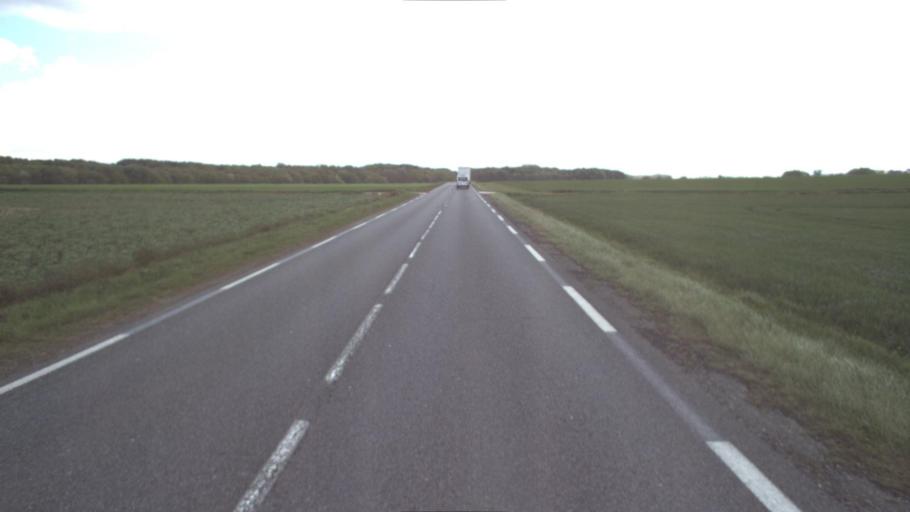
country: FR
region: Ile-de-France
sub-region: Departement de Seine-et-Marne
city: Jouy-le-Chatel
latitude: 48.6893
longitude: 3.1362
